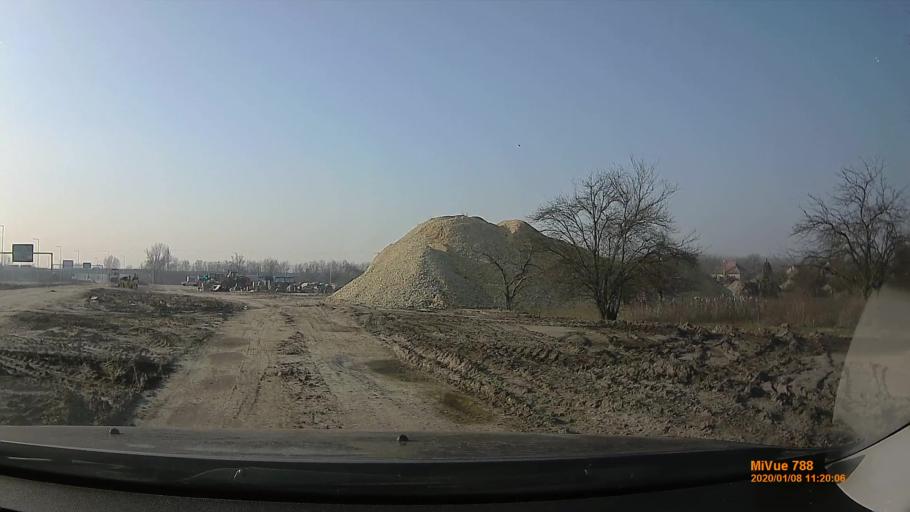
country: HU
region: Bacs-Kiskun
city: Helvecia
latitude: 46.8522
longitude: 19.6656
